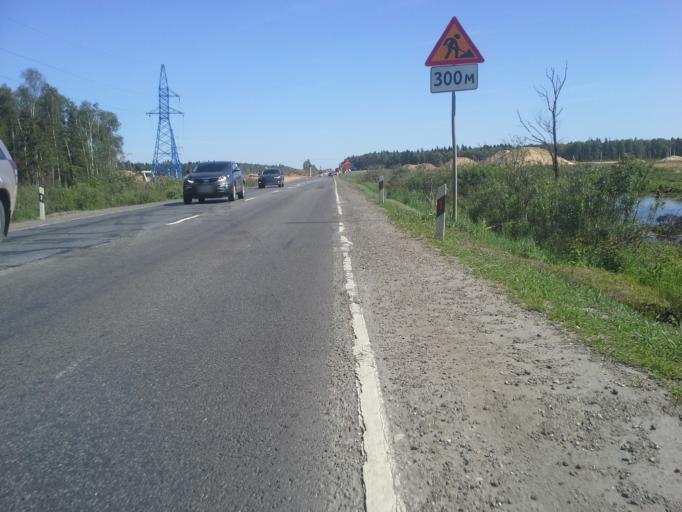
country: RU
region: Moskovskaya
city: Aprelevka
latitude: 55.4549
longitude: 37.1138
